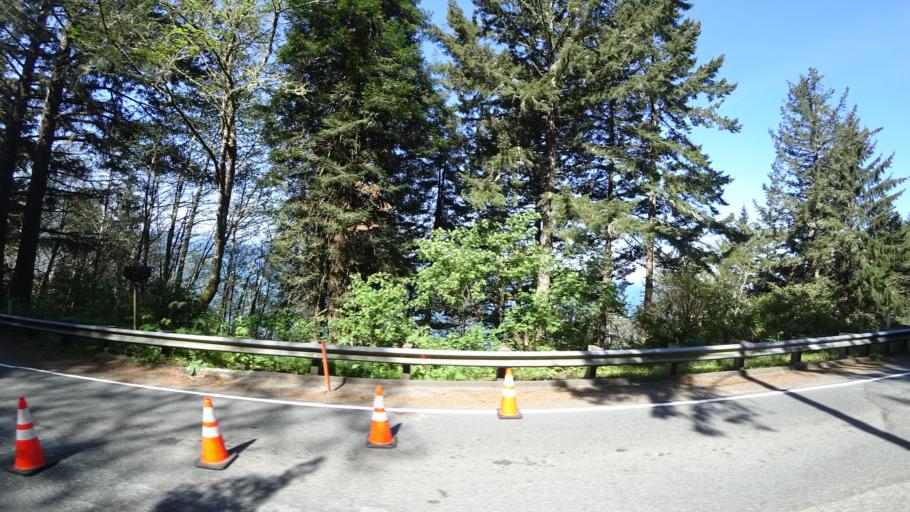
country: US
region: California
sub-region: Del Norte County
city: Bertsch-Oceanview
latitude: 41.6360
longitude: -124.1152
